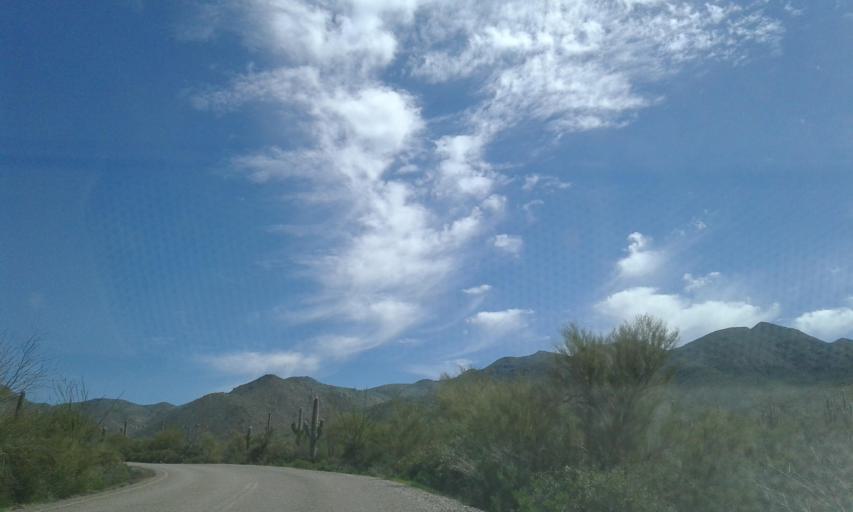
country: US
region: Arizona
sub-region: Gila County
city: Tonto Basin
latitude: 33.6239
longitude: -111.1998
